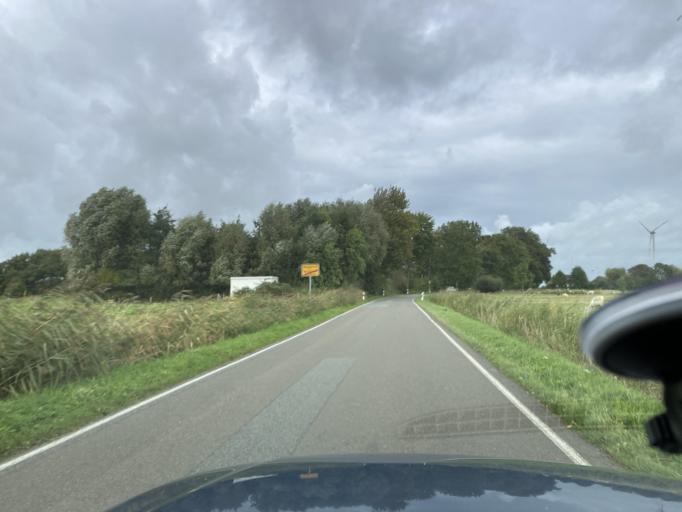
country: DE
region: Schleswig-Holstein
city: Wesselburener Deichhausen
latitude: 54.1805
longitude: 8.9414
